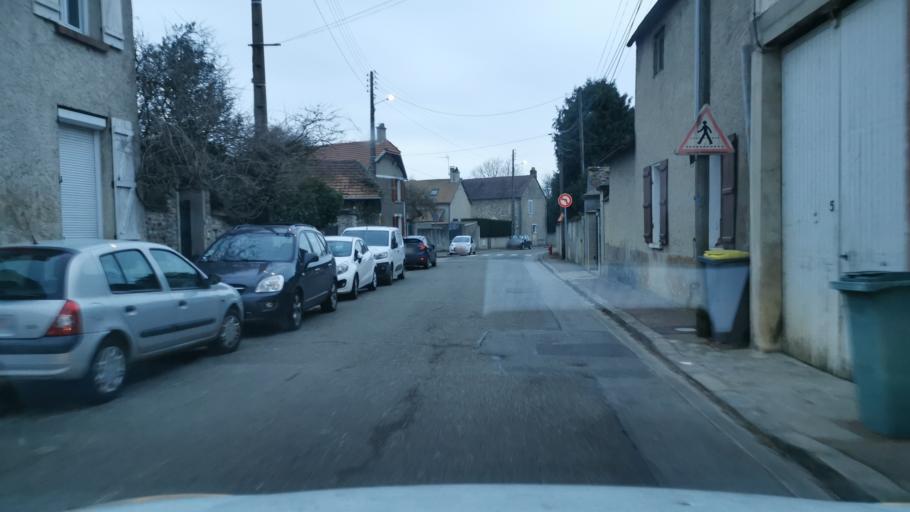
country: FR
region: Ile-de-France
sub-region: Departement des Yvelines
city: Longnes
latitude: 48.9215
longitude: 1.5876
